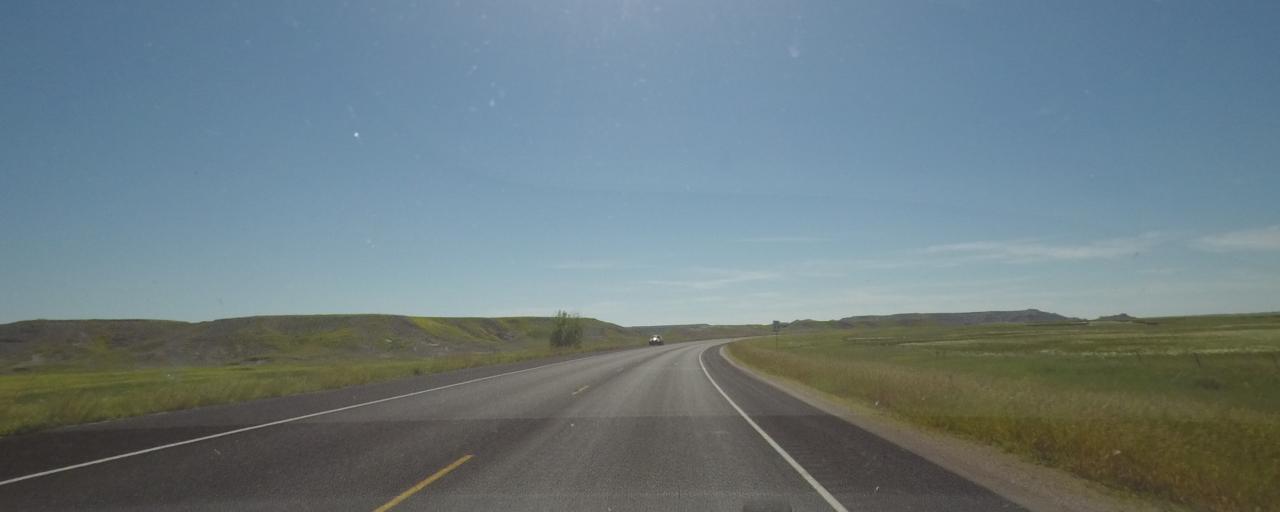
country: US
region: South Dakota
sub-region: Shannon County
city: Porcupine
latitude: 43.7782
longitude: -102.5364
